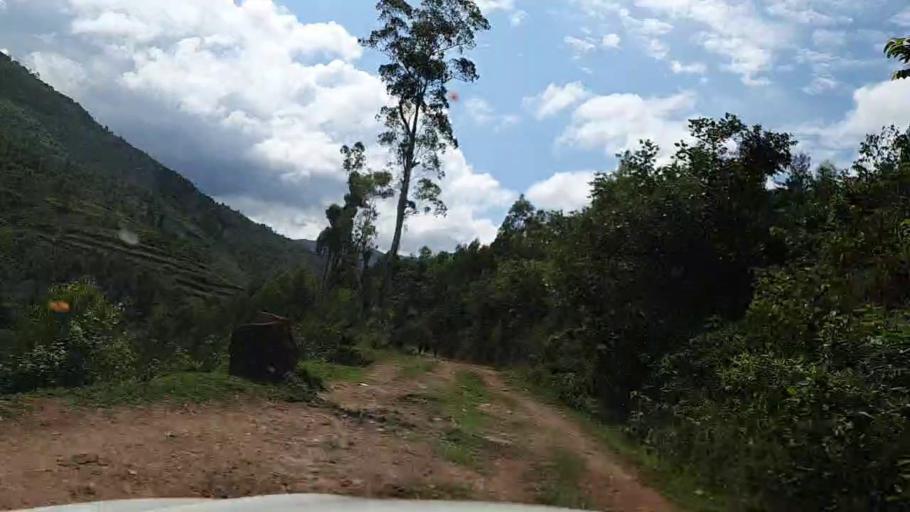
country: RW
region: Southern Province
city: Gikongoro
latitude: -2.3611
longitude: 29.5384
